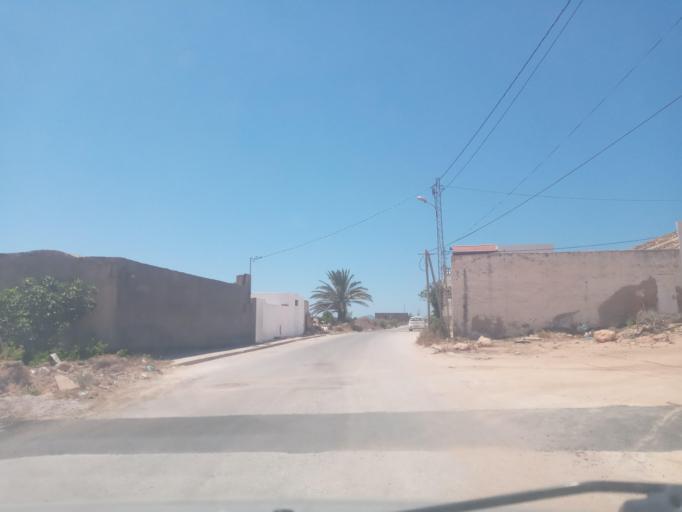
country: TN
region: Nabul
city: El Haouaria
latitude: 37.0510
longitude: 11.0000
